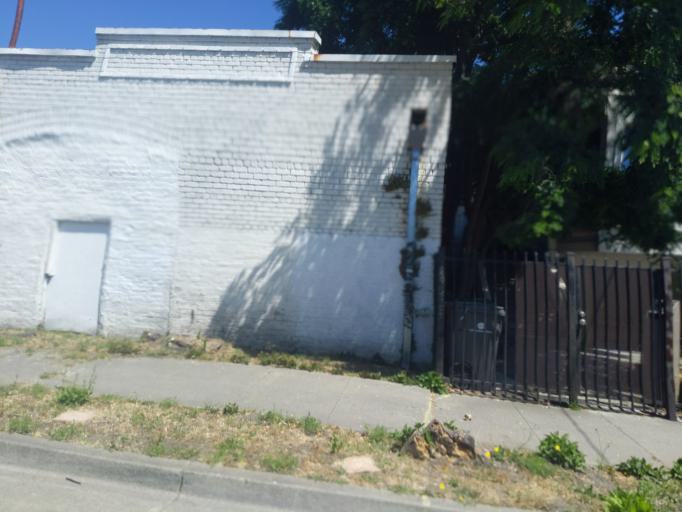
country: US
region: California
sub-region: Alameda County
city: Oakland
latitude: 37.8056
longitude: -122.2982
